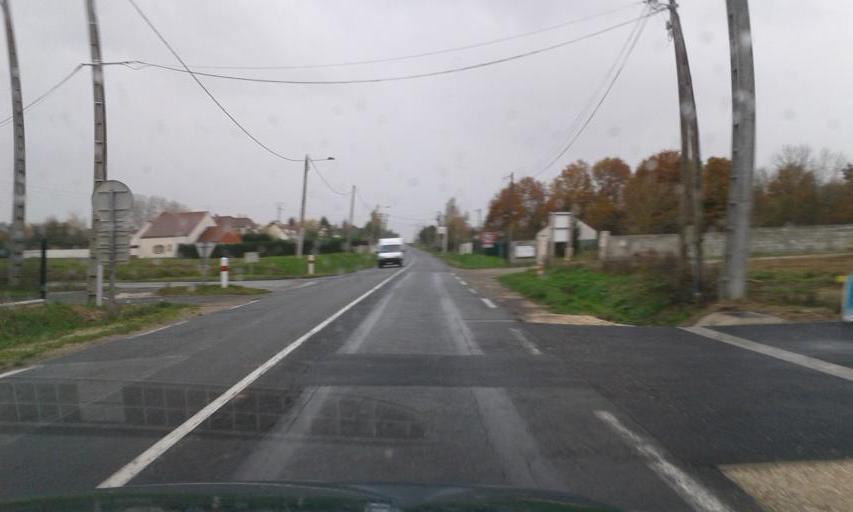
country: FR
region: Centre
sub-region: Departement du Loiret
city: Fay-aux-Loges
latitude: 47.9211
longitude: 2.1365
